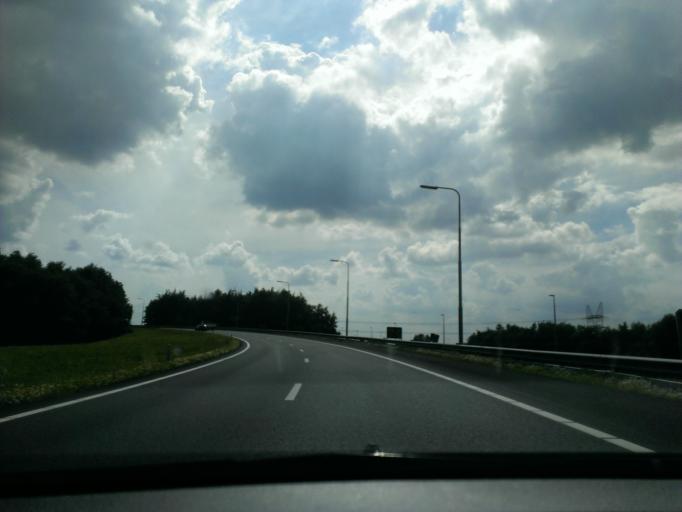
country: NL
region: Gelderland
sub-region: Gemeente Hattem
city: Hattem
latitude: 52.4871
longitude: 6.0202
